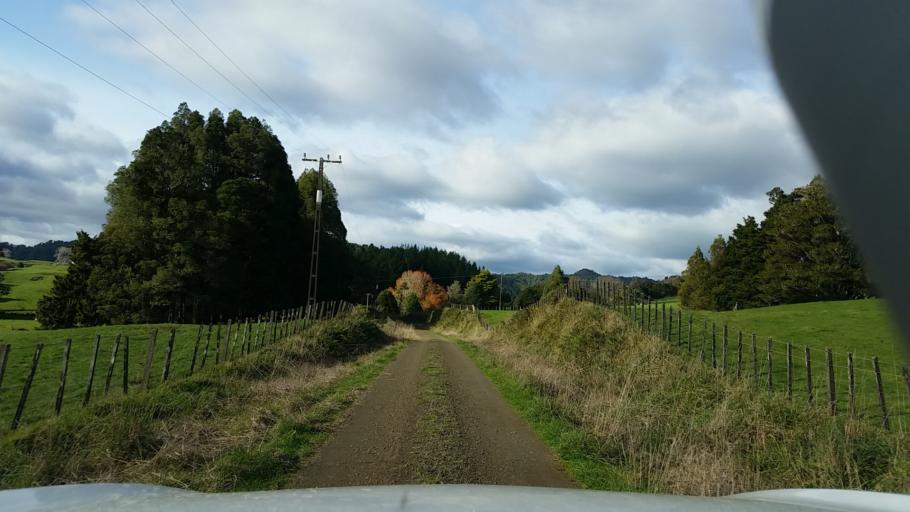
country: NZ
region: Taranaki
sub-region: New Plymouth District
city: Waitara
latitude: -38.9742
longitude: 174.5573
